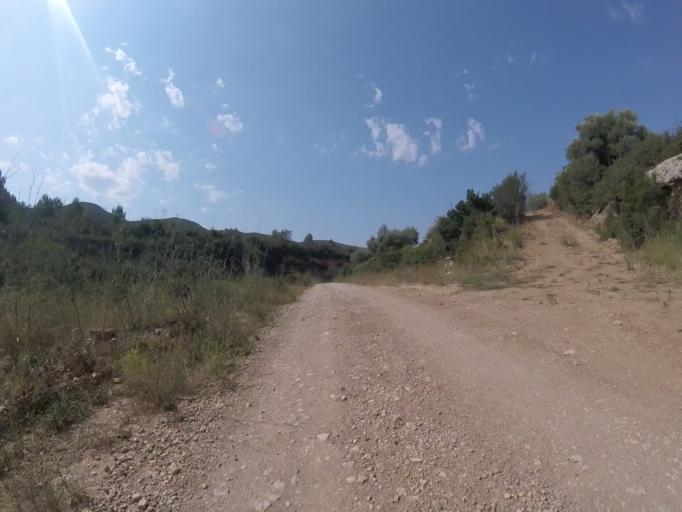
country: ES
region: Valencia
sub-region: Provincia de Castello
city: Alcala de Xivert
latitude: 40.3138
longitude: 0.1792
